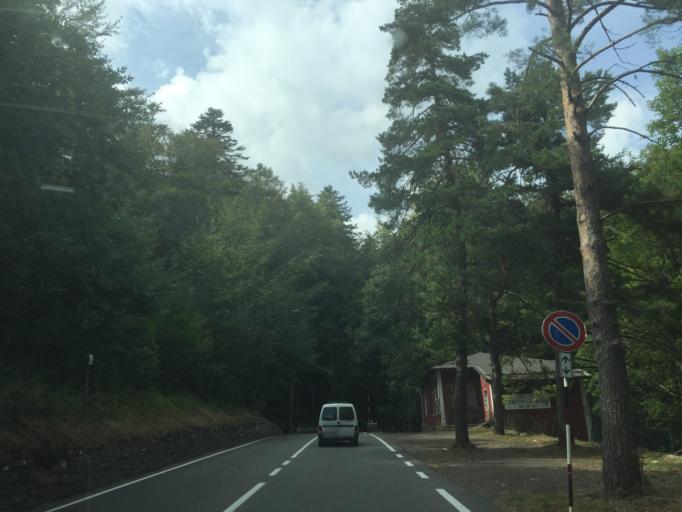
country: IT
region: Tuscany
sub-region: Provincia di Pistoia
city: Abetone
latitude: 44.1330
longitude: 10.6839
